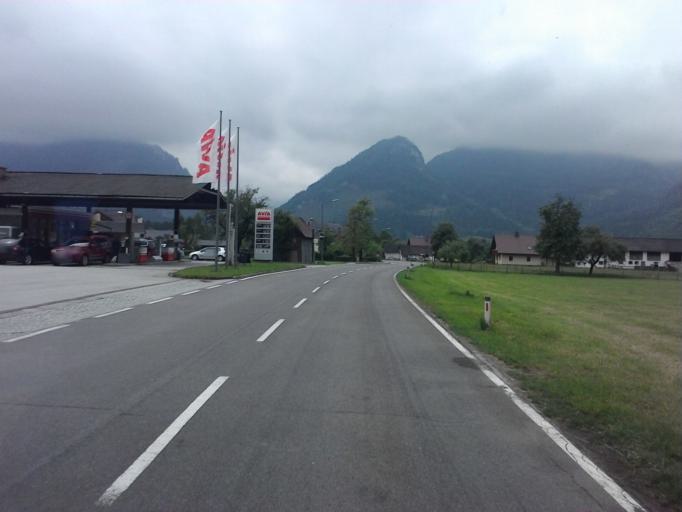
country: AT
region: Styria
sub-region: Politischer Bezirk Liezen
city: Gams bei Hieflau
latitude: 47.6544
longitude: 14.7644
